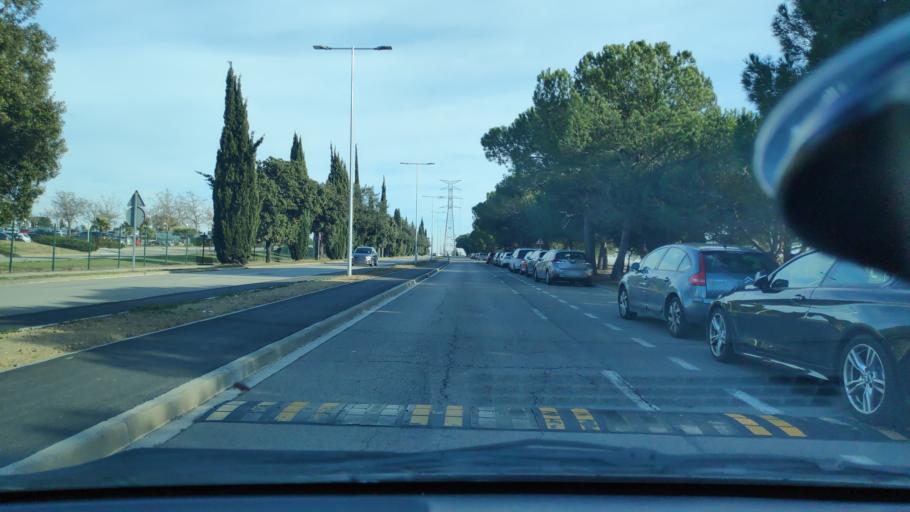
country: ES
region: Catalonia
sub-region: Provincia de Barcelona
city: Rubi
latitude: 41.4905
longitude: 2.0624
